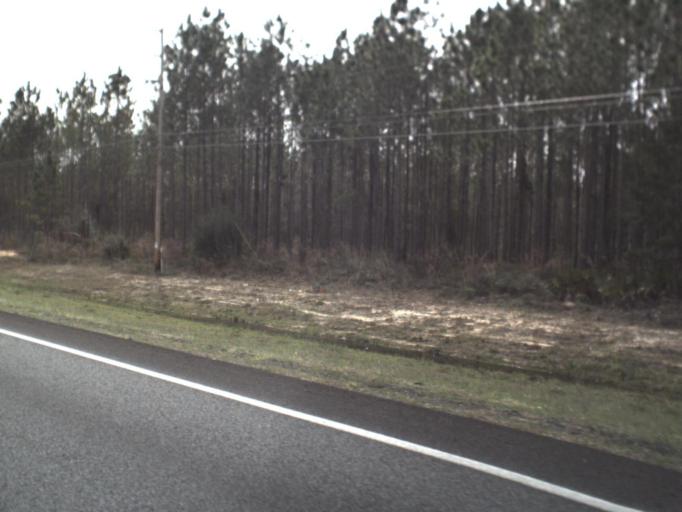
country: US
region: Florida
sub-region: Bay County
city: Youngstown
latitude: 30.3981
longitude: -85.4351
